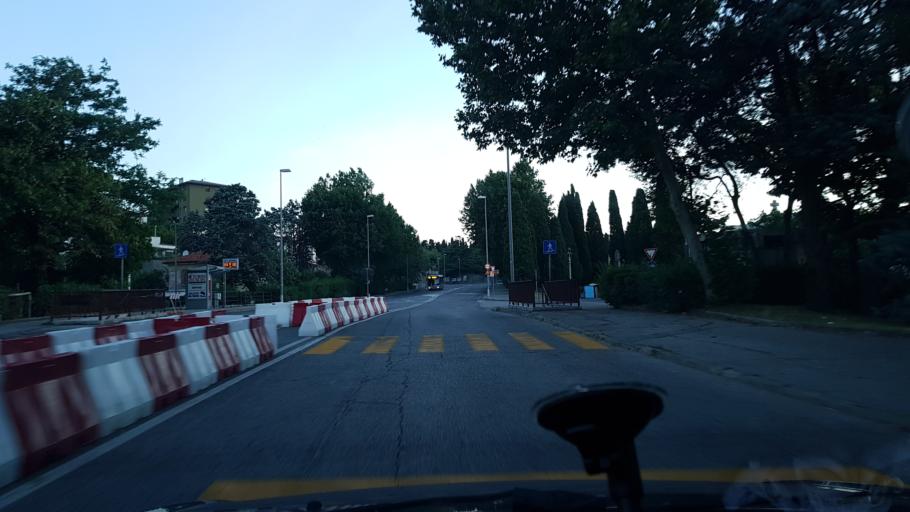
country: IT
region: Friuli Venezia Giulia
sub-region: Provincia di Trieste
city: Trieste
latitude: 45.6275
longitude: 13.7944
